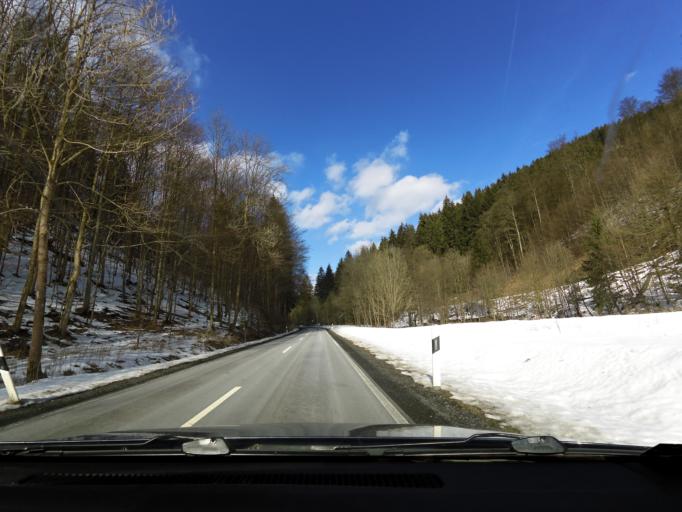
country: DE
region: Lower Saxony
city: Sankt Andreasberg
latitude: 51.6775
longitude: 10.5000
